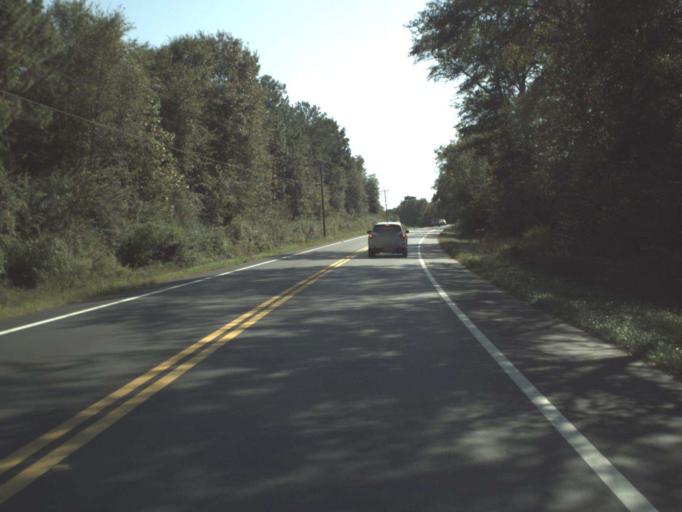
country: US
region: Alabama
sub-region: Covington County
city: Florala
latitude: 30.9253
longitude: -86.2800
